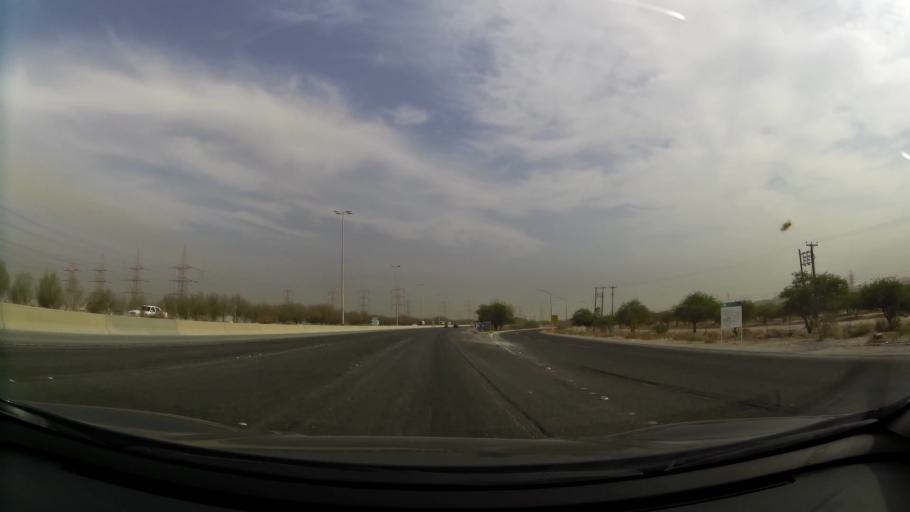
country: KW
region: Muhafazat al Jahra'
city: Al Jahra'
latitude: 29.3265
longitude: 47.7868
